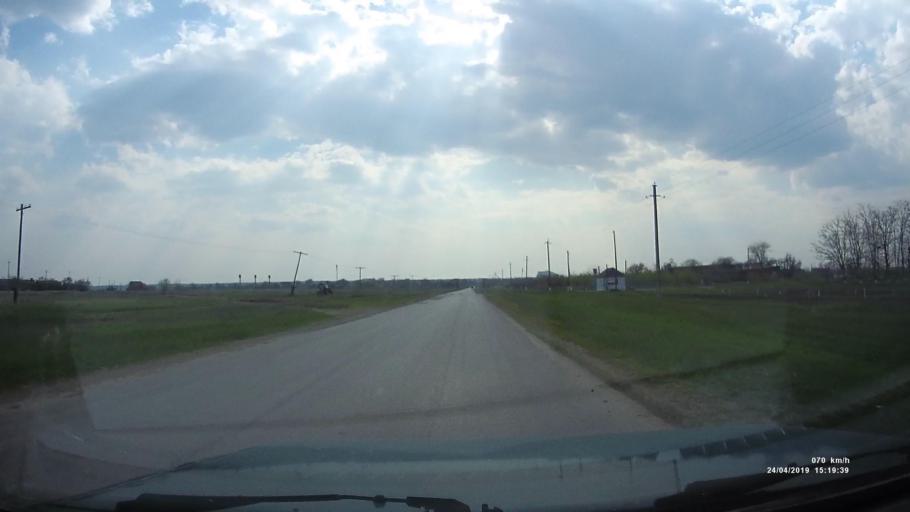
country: RU
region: Rostov
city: Remontnoye
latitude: 46.5388
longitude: 43.1427
